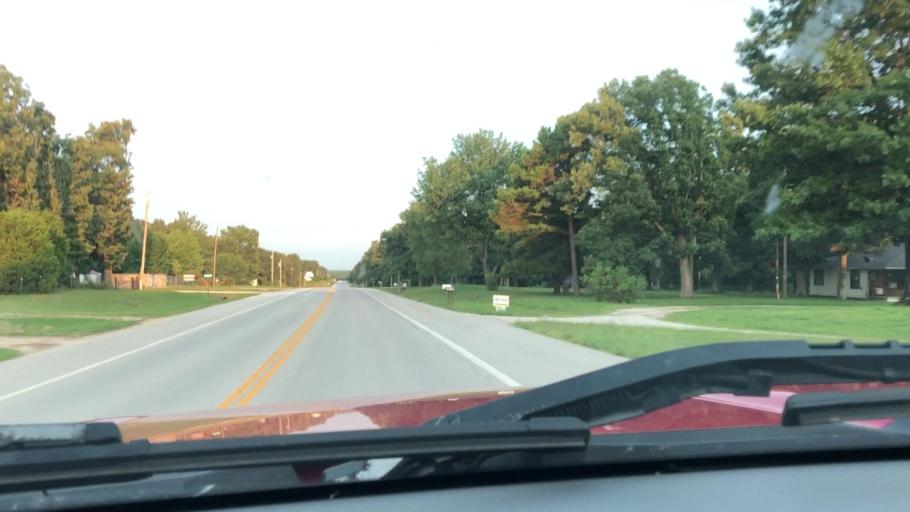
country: US
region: Missouri
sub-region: Jasper County
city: Duquesne
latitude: 36.9759
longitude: -94.4609
